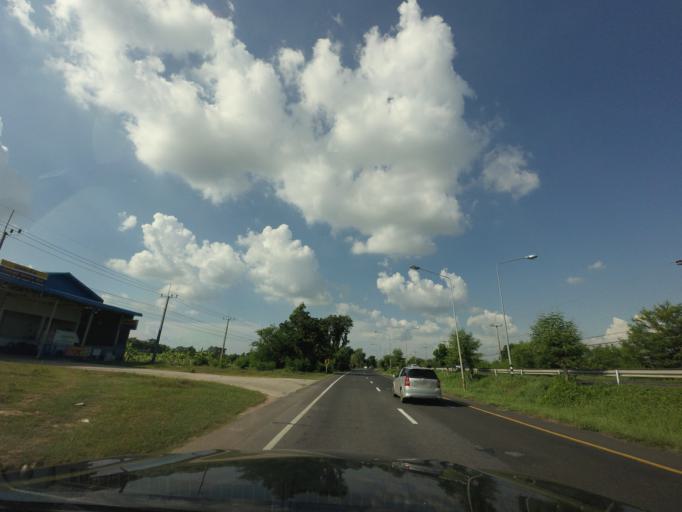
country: TH
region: Nakhon Ratchasima
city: Bua Lai
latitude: 15.6823
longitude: 102.5771
